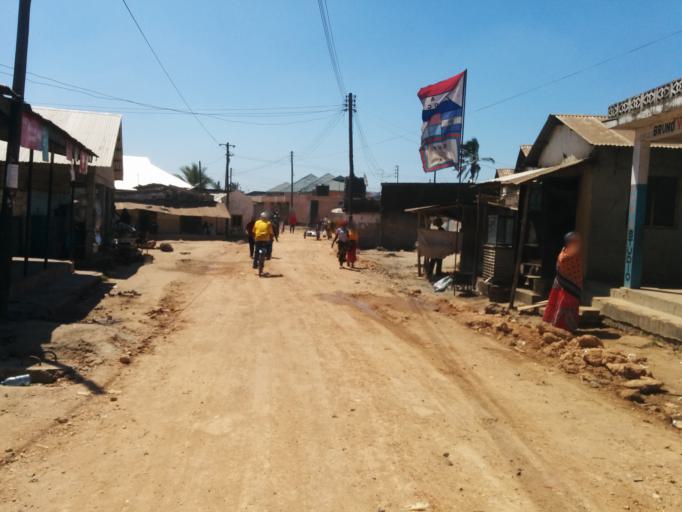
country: TZ
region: Dar es Salaam
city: Magomeni
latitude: -6.7933
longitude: 39.2422
